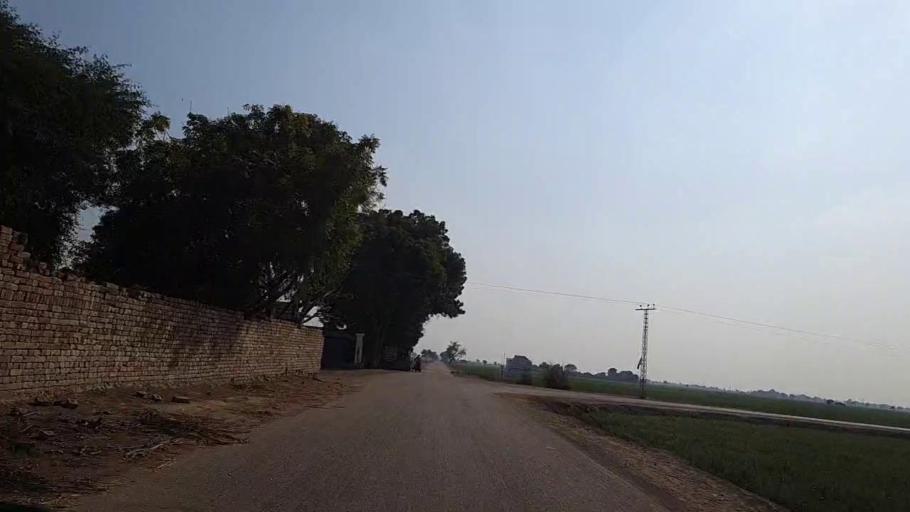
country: PK
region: Sindh
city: Sakrand
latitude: 26.0983
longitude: 68.2905
